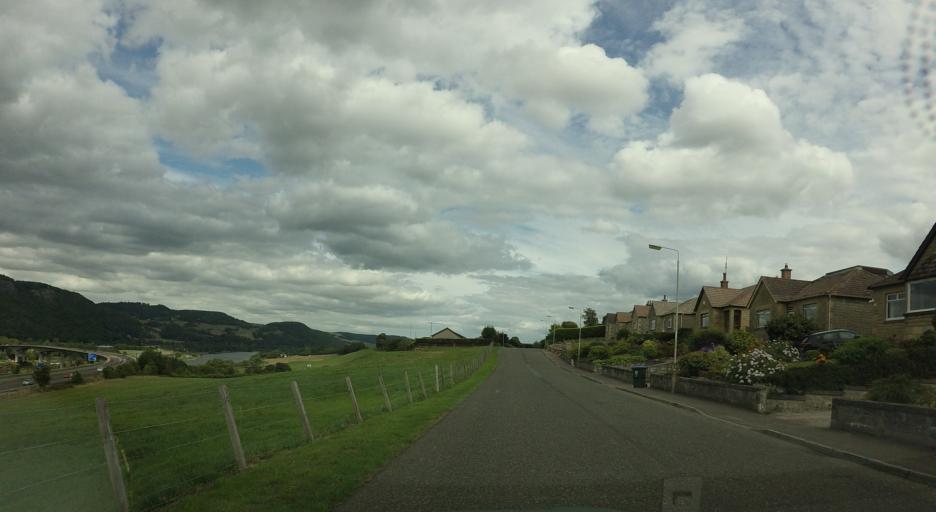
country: GB
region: Scotland
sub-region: Perth and Kinross
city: Bridge of Earn
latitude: 56.3725
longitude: -3.4175
